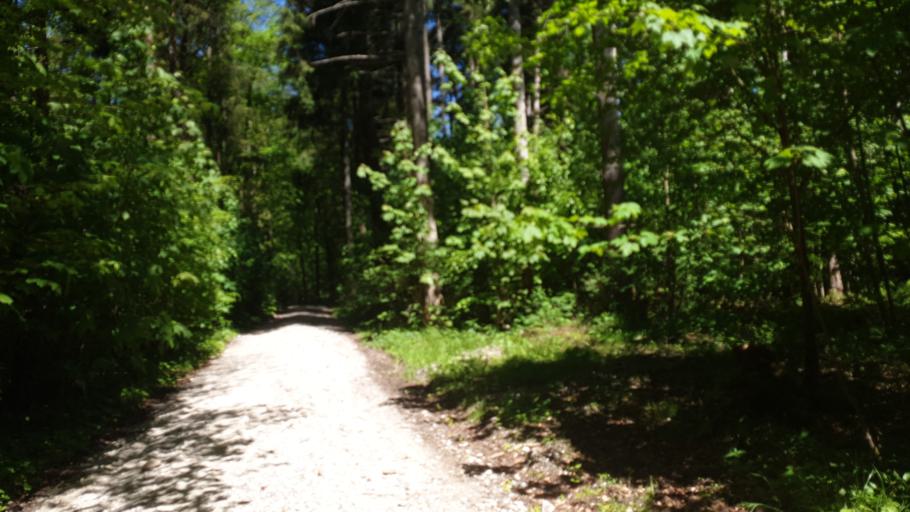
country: DE
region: Bavaria
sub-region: Upper Bavaria
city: Seeshaupt
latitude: 47.8015
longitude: 11.2883
